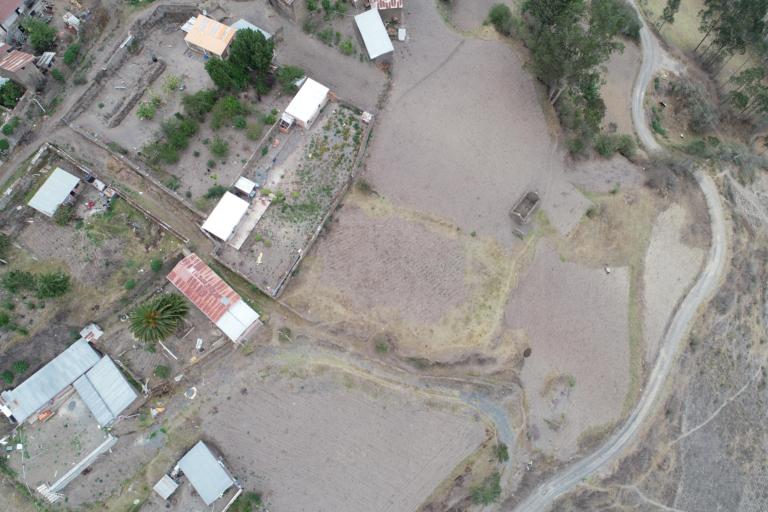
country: BO
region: La Paz
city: Sorata
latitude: -15.6362
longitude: -68.7046
